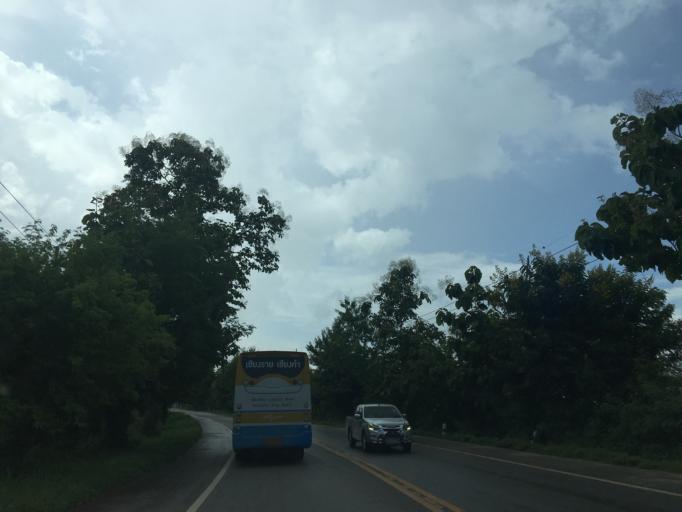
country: TH
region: Chiang Rai
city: Wiang Chai
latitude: 19.7919
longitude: 99.9090
